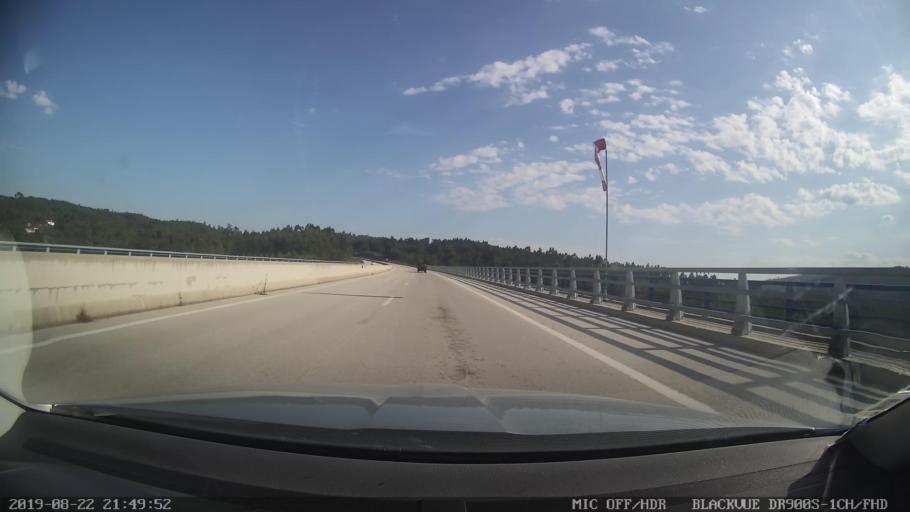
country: PT
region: Coimbra
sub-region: Penela
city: Penela
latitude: 40.0528
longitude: -8.3719
